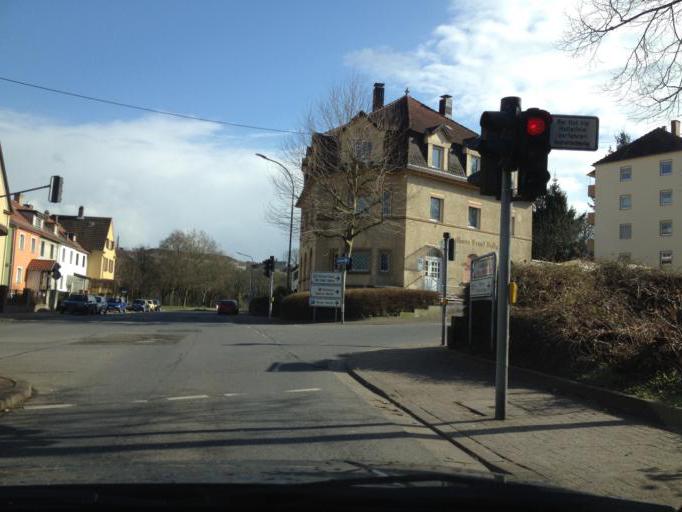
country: DE
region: Saarland
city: Neunkirchen
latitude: 49.3469
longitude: 7.1880
